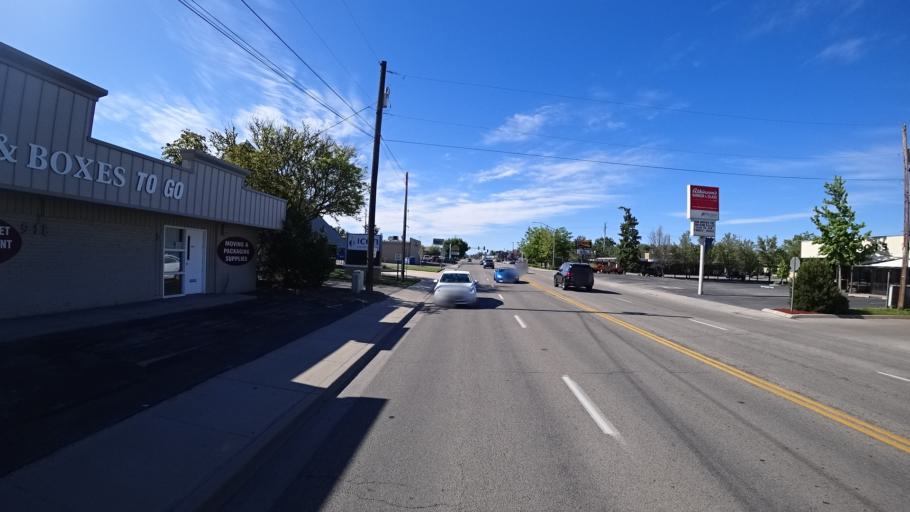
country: US
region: Idaho
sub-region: Ada County
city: Garden City
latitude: 43.6131
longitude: -116.2434
